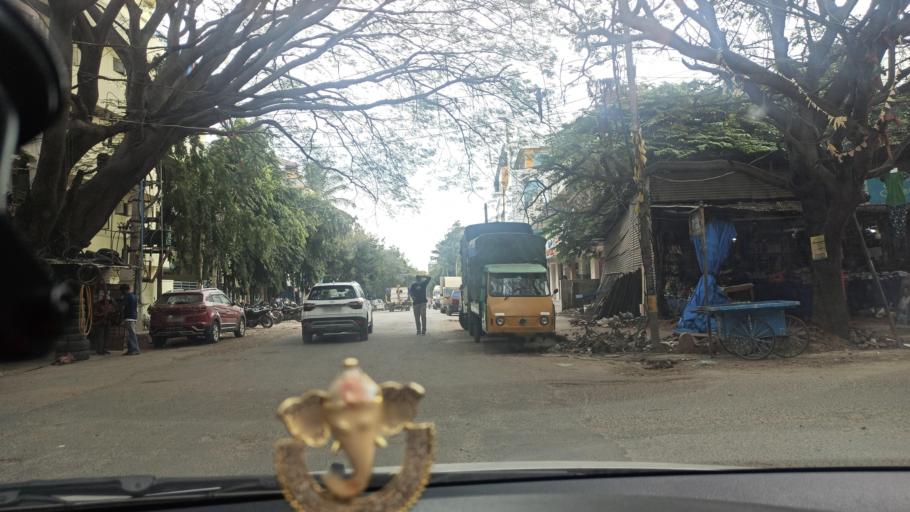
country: IN
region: Karnataka
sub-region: Bangalore Urban
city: Bangalore
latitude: 12.9195
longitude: 77.6489
